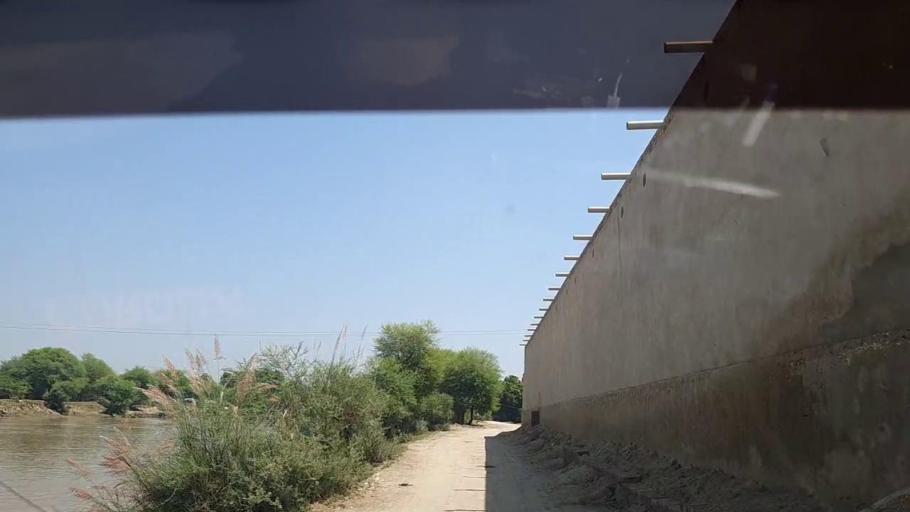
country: PK
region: Sindh
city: Ghauspur
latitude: 28.1643
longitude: 69.1339
